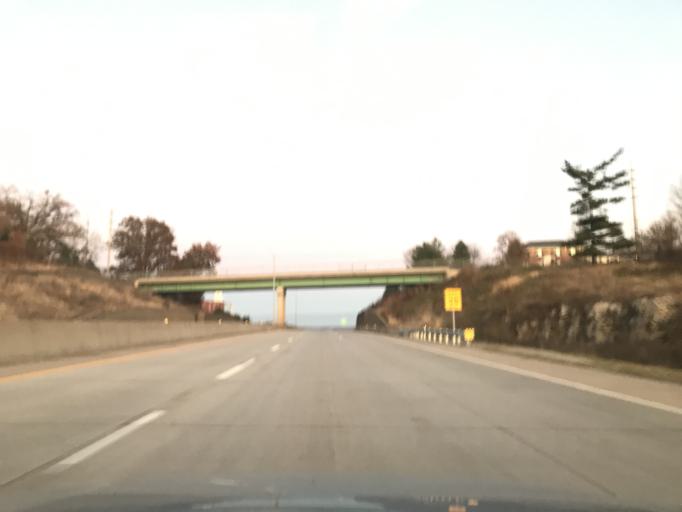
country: US
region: Missouri
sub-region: Marion County
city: Hannibal
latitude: 39.7158
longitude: -91.3792
